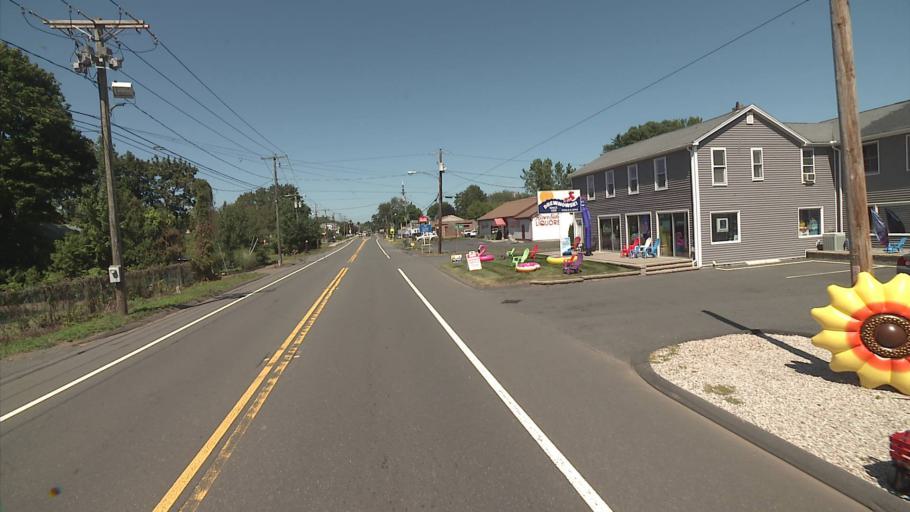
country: US
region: Massachusetts
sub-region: Hampden County
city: Agawam
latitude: 42.0313
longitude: -72.6169
